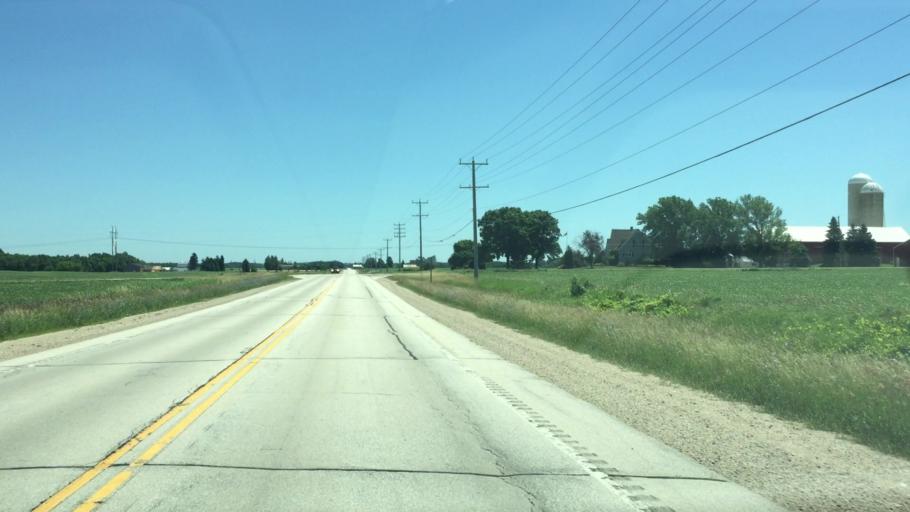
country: US
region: Wisconsin
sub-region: Calumet County
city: Sherwood
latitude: 44.1406
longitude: -88.2265
